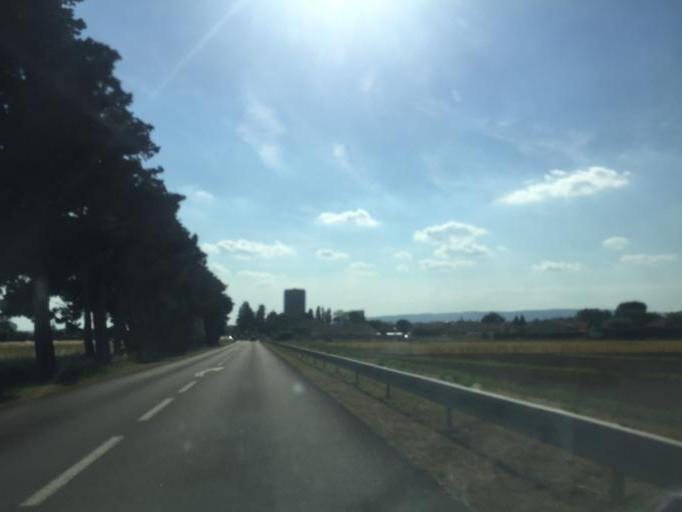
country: FR
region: Rhone-Alpes
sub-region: Departement de la Drome
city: Pierrelatte
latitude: 44.3801
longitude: 4.7128
